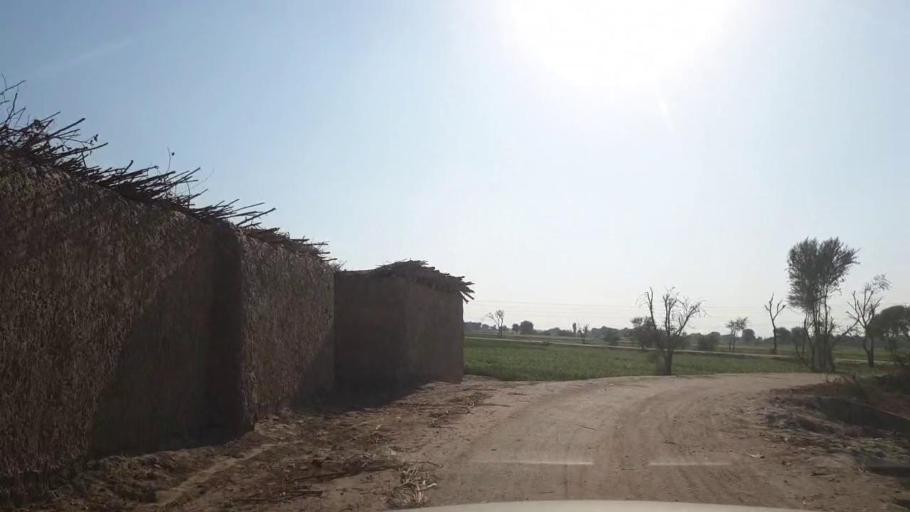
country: PK
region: Sindh
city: Tando Adam
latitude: 25.6877
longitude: 68.6893
